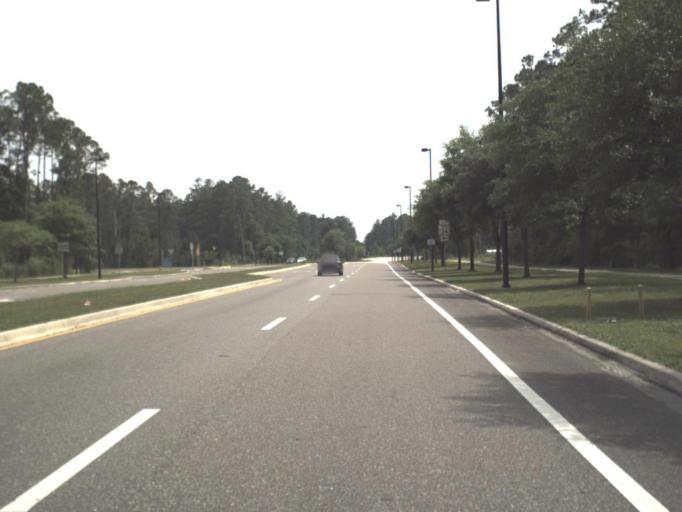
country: US
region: Florida
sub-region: Duval County
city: Baldwin
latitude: 30.2475
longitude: -81.8866
